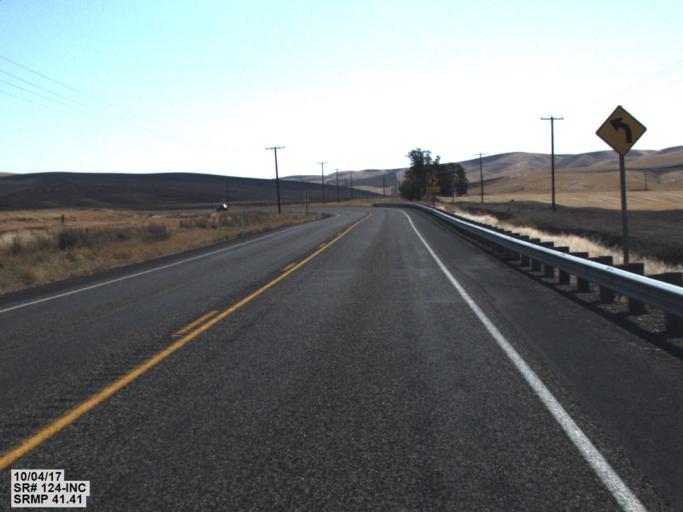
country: US
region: Washington
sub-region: Walla Walla County
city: Waitsburg
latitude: 46.2708
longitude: -118.2212
